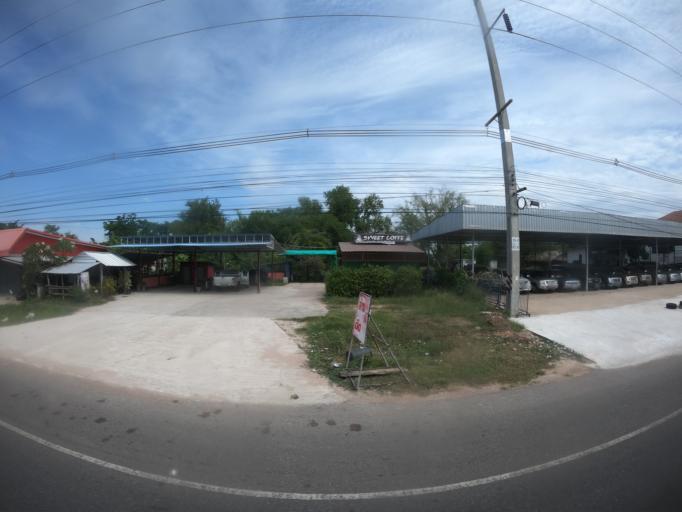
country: TH
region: Maha Sarakham
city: Chiang Yuen
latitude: 16.4142
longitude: 103.0870
